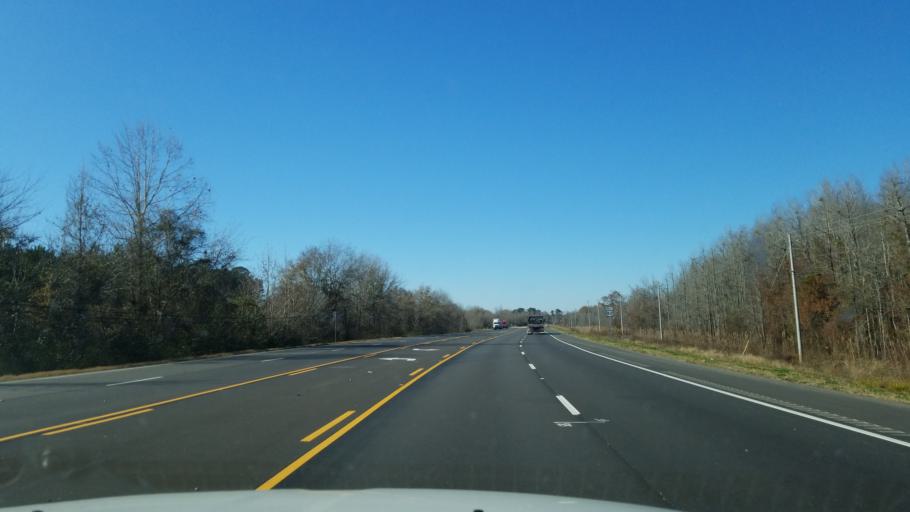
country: US
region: Alabama
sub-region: Pickens County
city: Reform
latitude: 33.3724
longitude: -87.9998
